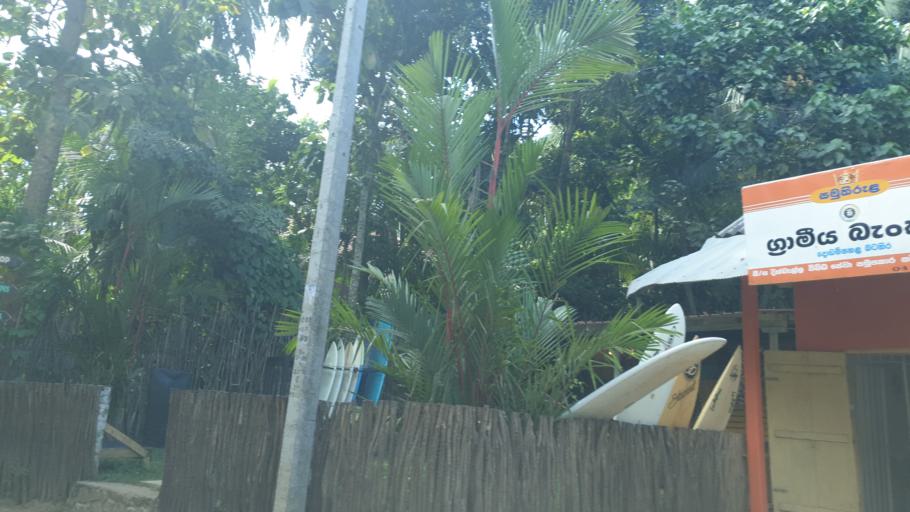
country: LK
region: Southern
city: Tangalla
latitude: 5.9661
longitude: 80.7074
